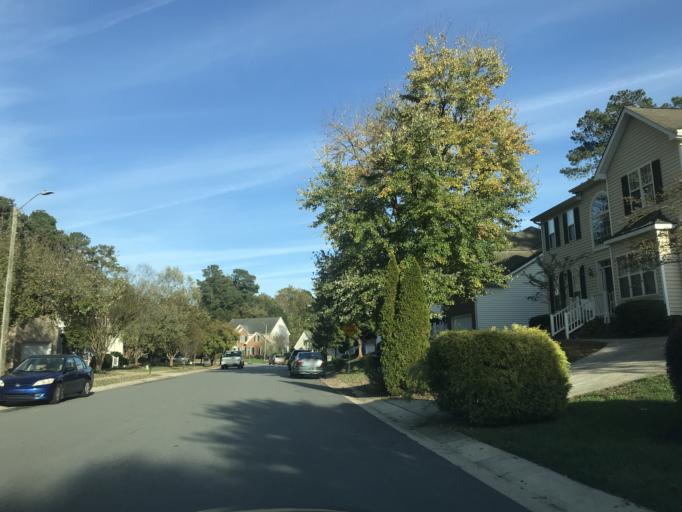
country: US
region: North Carolina
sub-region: Wake County
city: Rolesville
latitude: 35.8910
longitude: -78.5467
